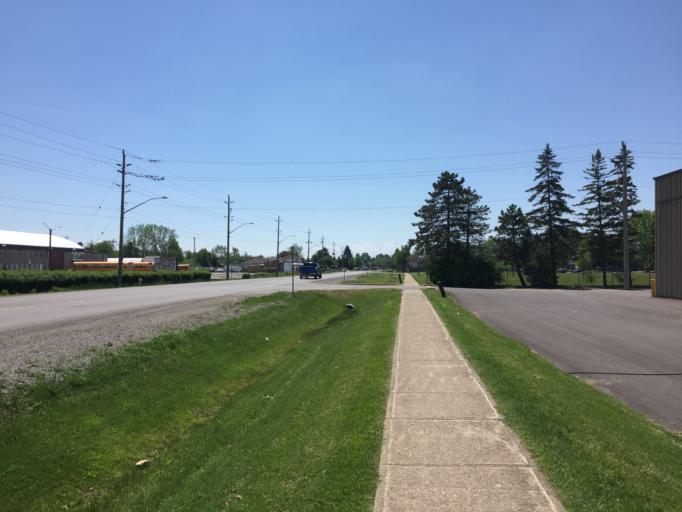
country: CA
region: Ontario
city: Port Colborne
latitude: 42.8957
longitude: -79.2653
